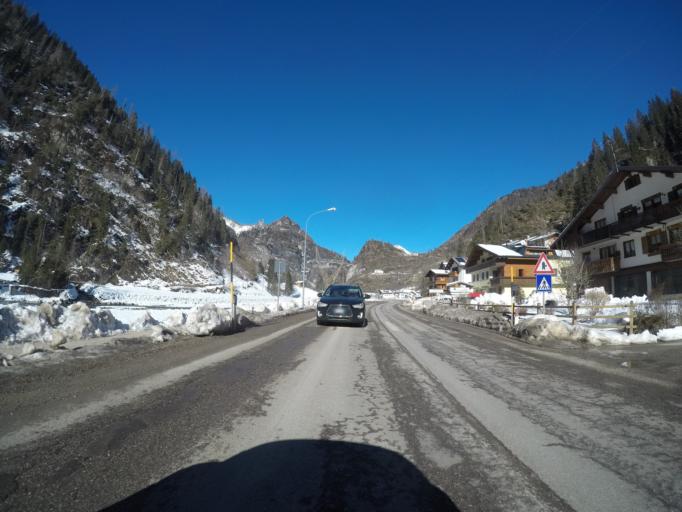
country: IT
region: Veneto
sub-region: Provincia di Belluno
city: Rocca Pietore
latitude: 46.4338
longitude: 11.9976
